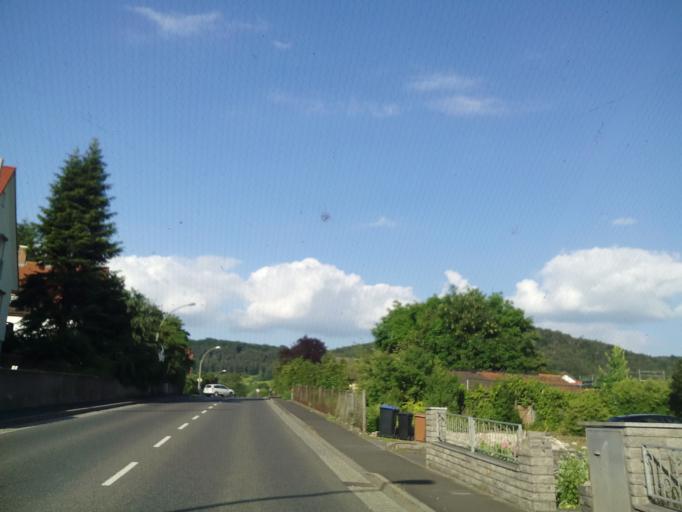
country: DE
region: Bavaria
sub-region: Regierungsbezirk Unterfranken
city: Bad Kissingen
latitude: 50.2053
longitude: 10.0957
